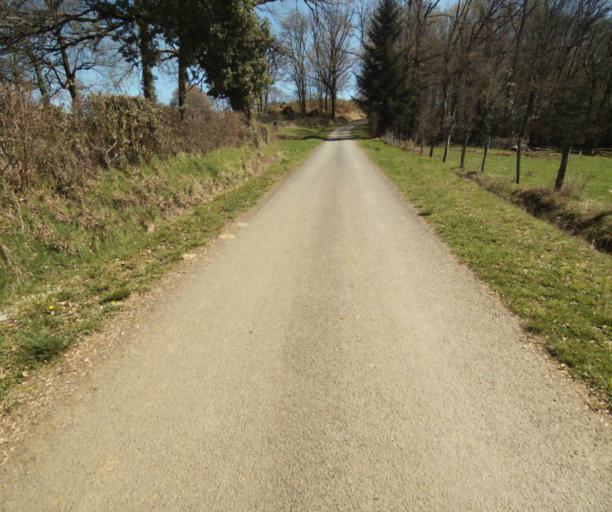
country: FR
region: Limousin
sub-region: Departement de la Correze
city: Saint-Clement
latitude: 45.3719
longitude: 1.6794
